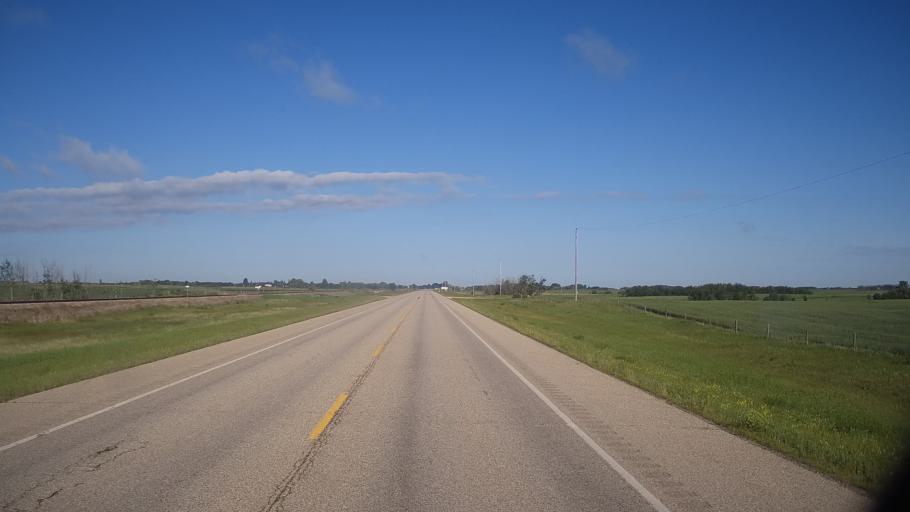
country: CA
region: Saskatchewan
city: Lanigan
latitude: 51.8682
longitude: -105.1564
